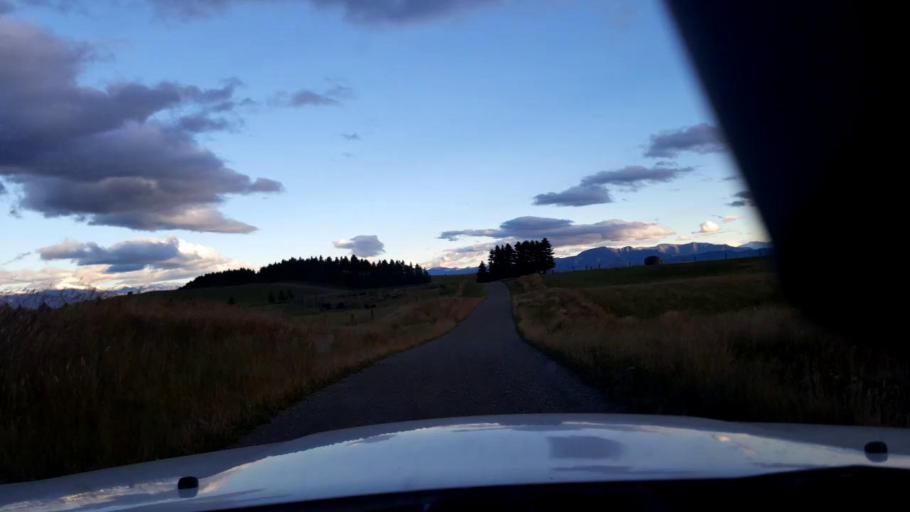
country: NZ
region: Canterbury
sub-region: Timaru District
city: Pleasant Point
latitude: -44.2641
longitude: 170.9183
